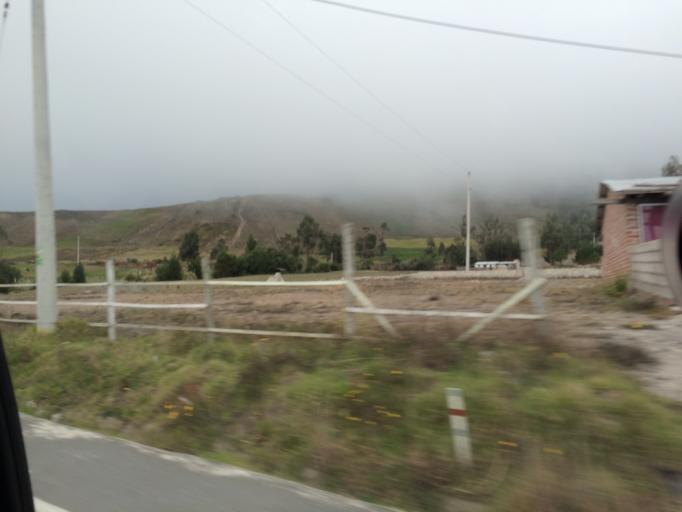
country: EC
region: Chimborazo
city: Alausi
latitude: -2.0782
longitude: -78.7352
